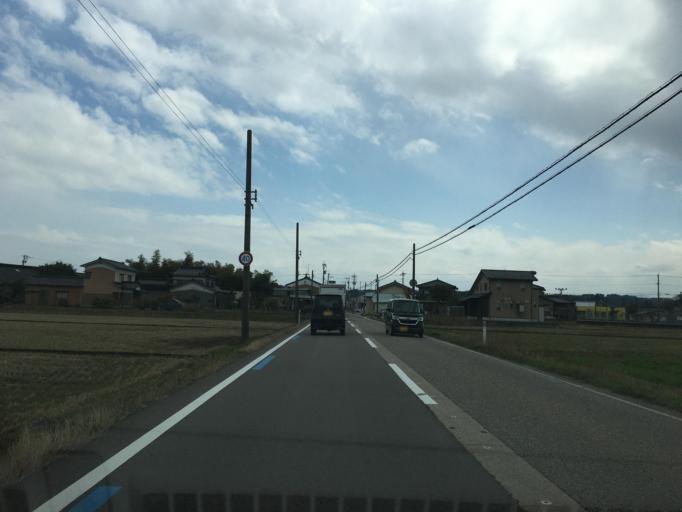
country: JP
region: Toyama
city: Kuragaki-kosugi
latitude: 36.6905
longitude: 137.1173
